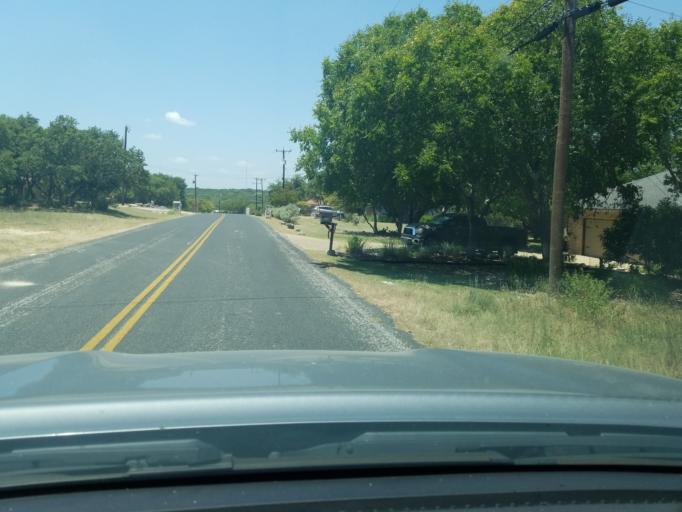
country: US
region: Texas
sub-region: Bexar County
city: Timberwood Park
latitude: 29.6955
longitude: -98.4879
